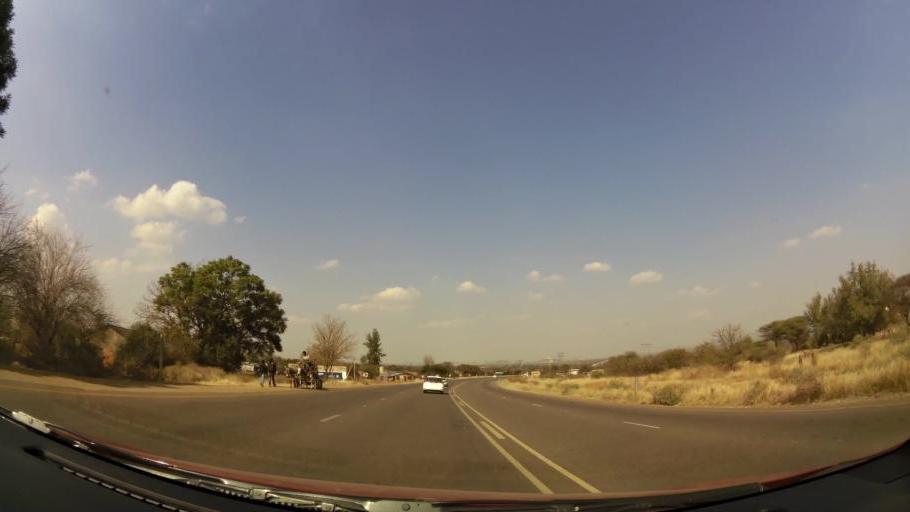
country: ZA
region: North-West
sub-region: Bojanala Platinum District Municipality
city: Mogwase
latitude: -25.3836
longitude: 27.0673
